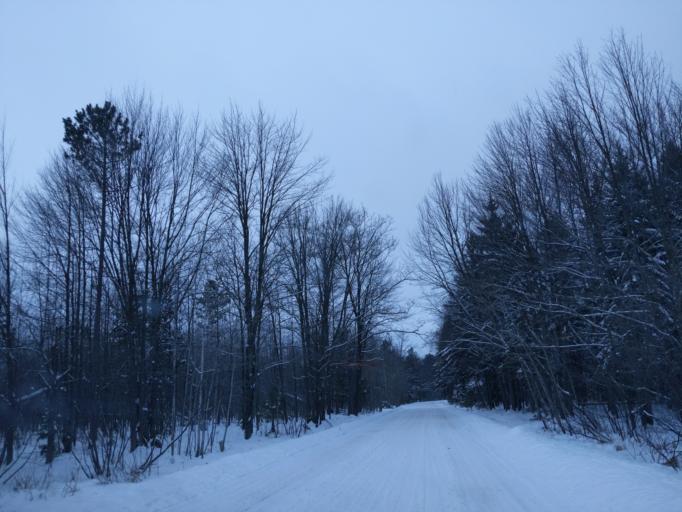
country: US
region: Wisconsin
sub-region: Marathon County
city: Mosinee
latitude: 44.7603
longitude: -89.8654
